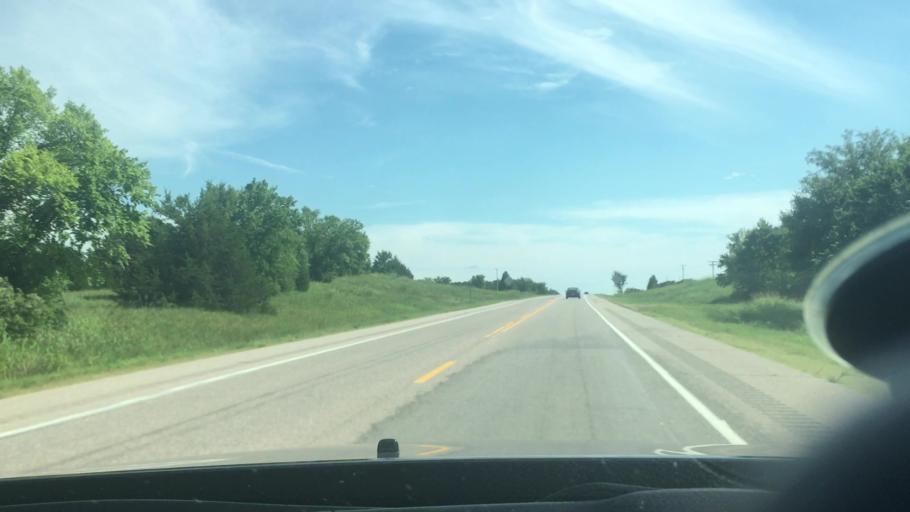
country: US
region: Oklahoma
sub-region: Seminole County
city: Maud
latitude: 35.0722
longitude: -96.6788
